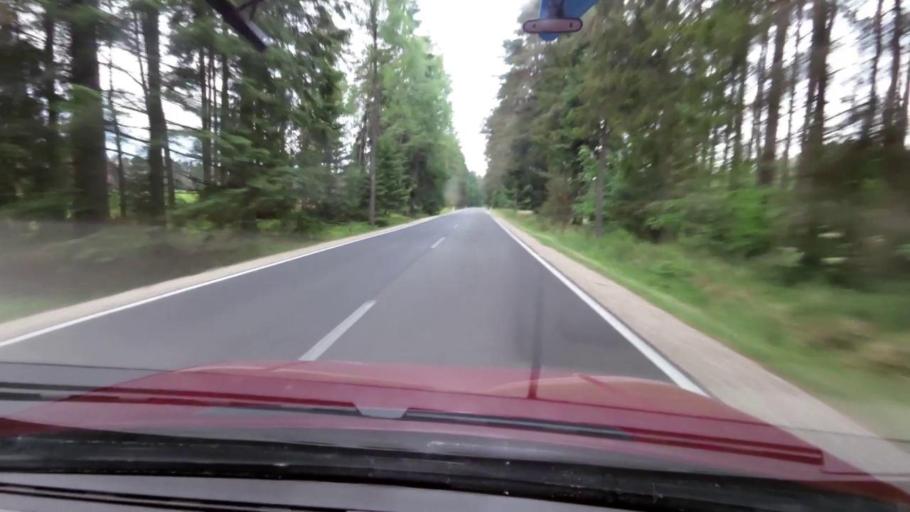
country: PL
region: West Pomeranian Voivodeship
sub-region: Powiat koszalinski
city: Polanow
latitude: 54.1448
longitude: 16.4810
